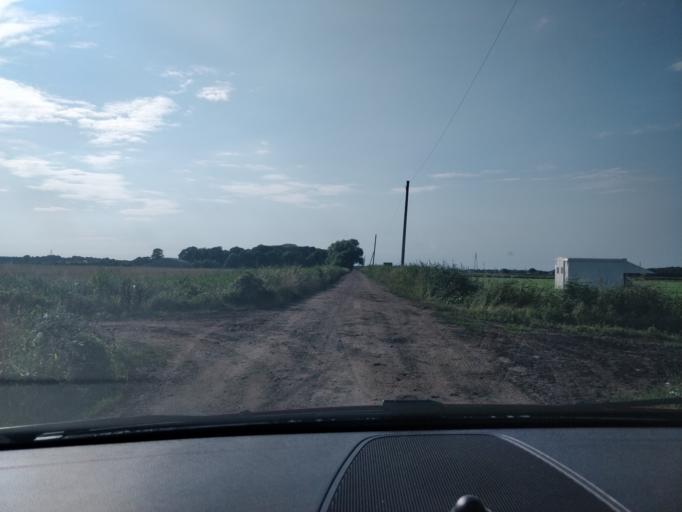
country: GB
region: England
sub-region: Lancashire
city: Banks
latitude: 53.6528
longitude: -2.9181
